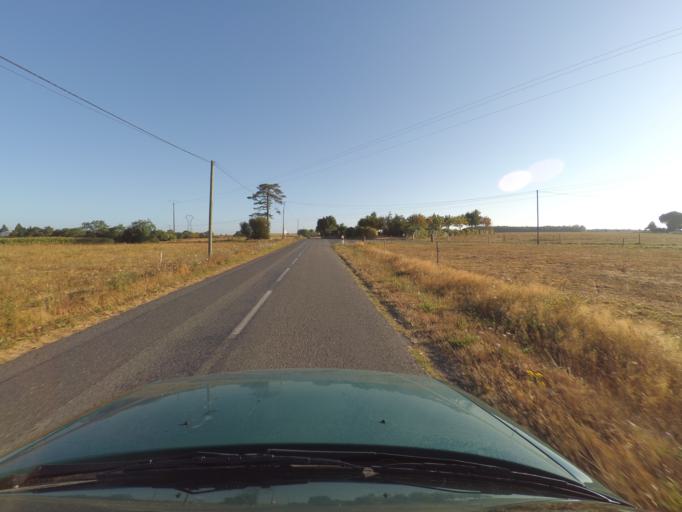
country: FR
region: Pays de la Loire
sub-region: Departement de la Loire-Atlantique
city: Le Bignon
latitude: 47.0803
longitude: -1.4675
